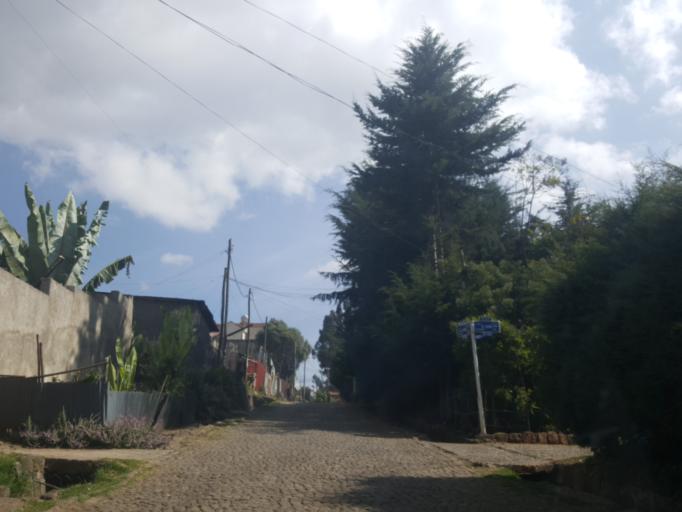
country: ET
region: Adis Abeba
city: Addis Ababa
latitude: 9.0534
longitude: 38.7246
